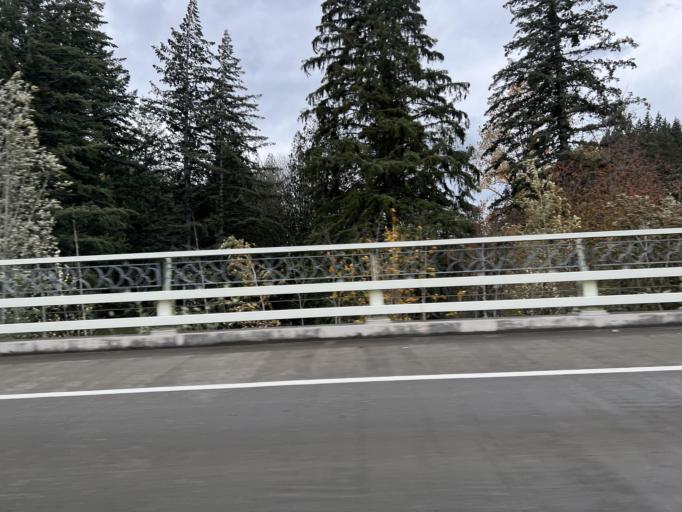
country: US
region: Washington
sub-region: King County
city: Tanner
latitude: 47.4870
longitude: -121.7595
